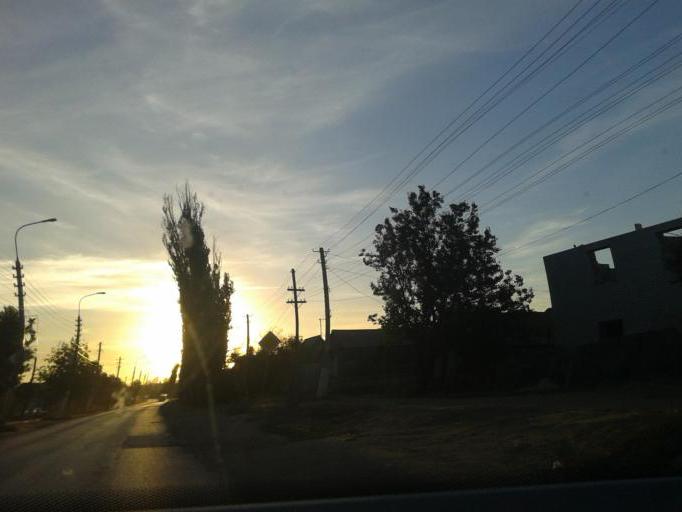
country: RU
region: Volgograd
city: Krasnoslobodsk
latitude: 48.7082
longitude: 44.5694
